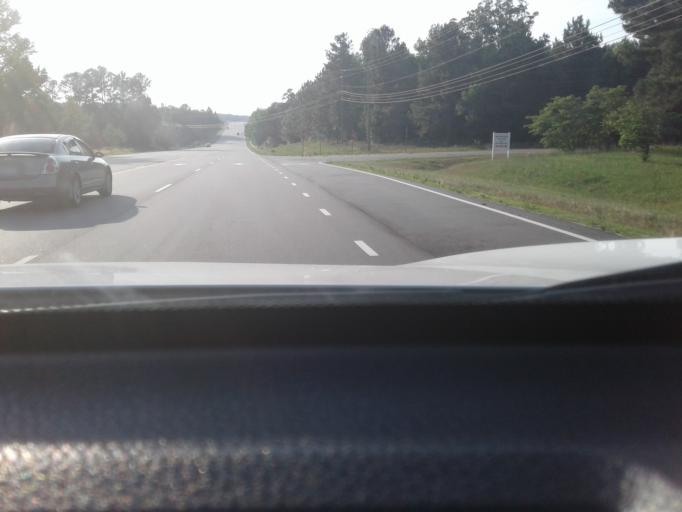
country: US
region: North Carolina
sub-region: Harnett County
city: Buies Creek
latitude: 35.3800
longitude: -78.7149
